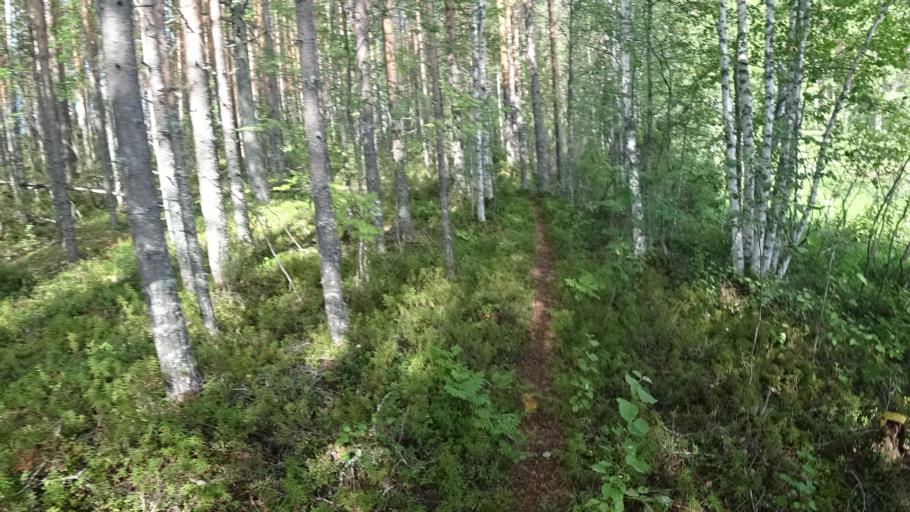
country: FI
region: North Karelia
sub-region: Joensuu
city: Ilomantsi
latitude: 62.6109
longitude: 31.1888
